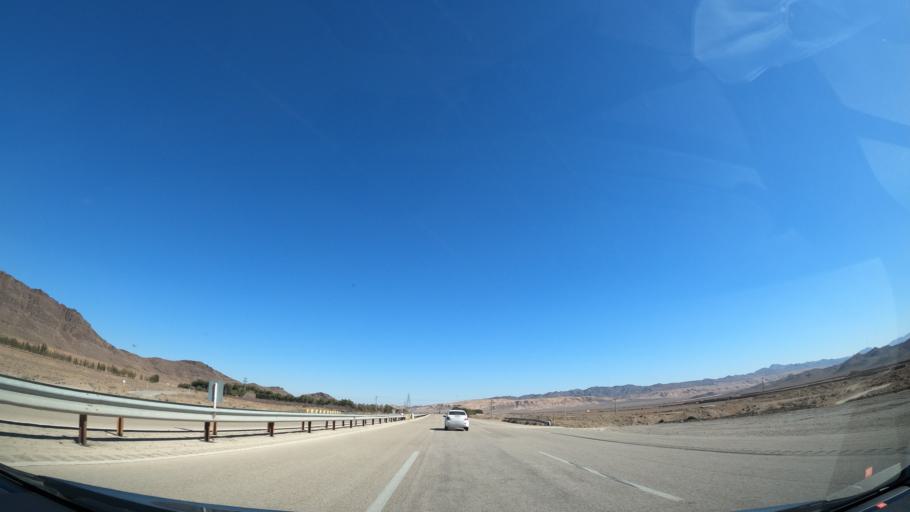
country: IR
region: Isfahan
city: Natanz
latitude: 33.3964
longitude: 51.9712
